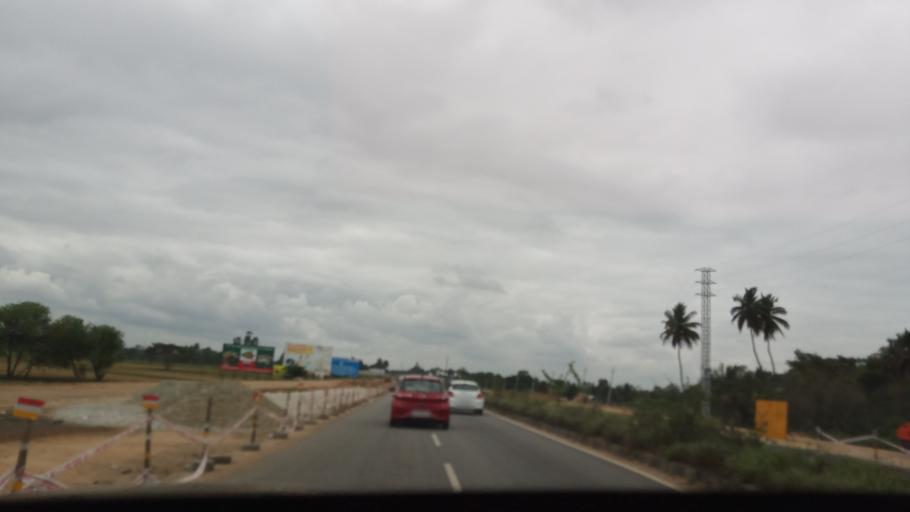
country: IN
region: Karnataka
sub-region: Mandya
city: Mandya
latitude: 12.5115
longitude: 76.8476
